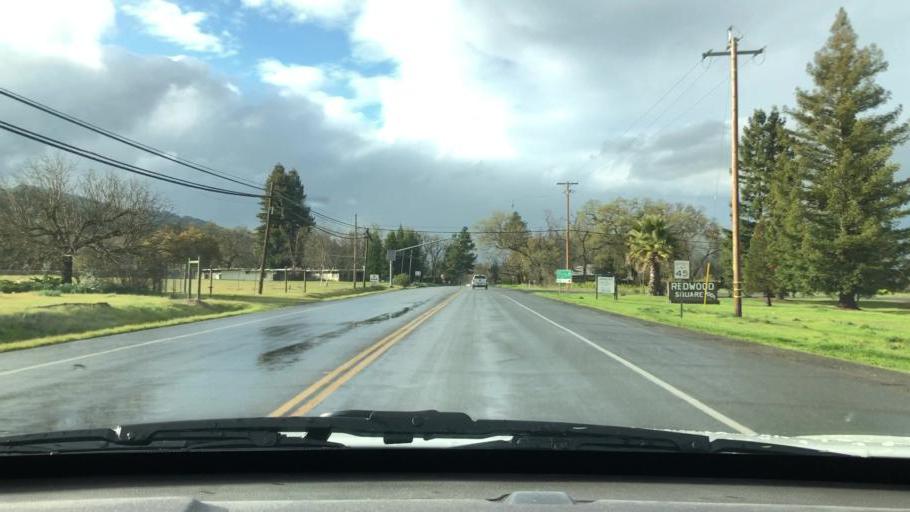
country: US
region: California
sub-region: Mendocino County
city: Talmage
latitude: 39.1110
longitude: -123.1973
